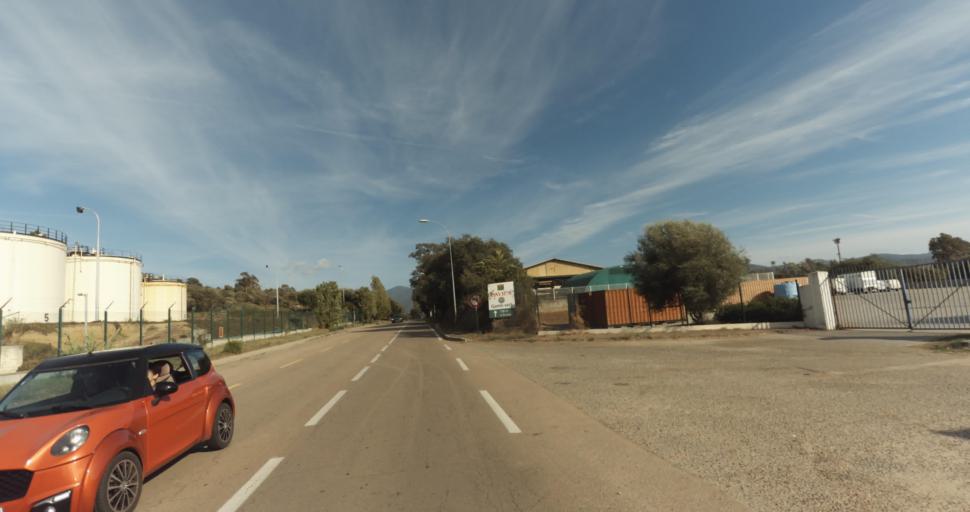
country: FR
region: Corsica
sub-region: Departement de la Corse-du-Sud
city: Afa
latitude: 41.9291
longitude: 8.7912
